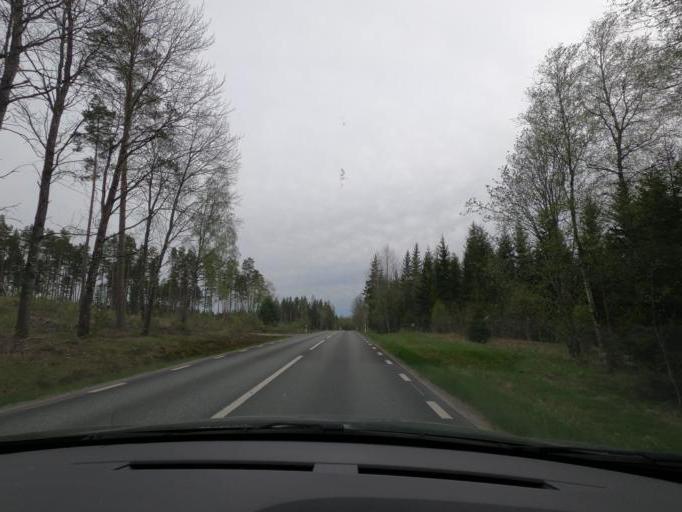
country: SE
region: Joenkoeping
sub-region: Varnamo Kommun
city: Bredaryd
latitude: 57.2100
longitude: 13.7670
